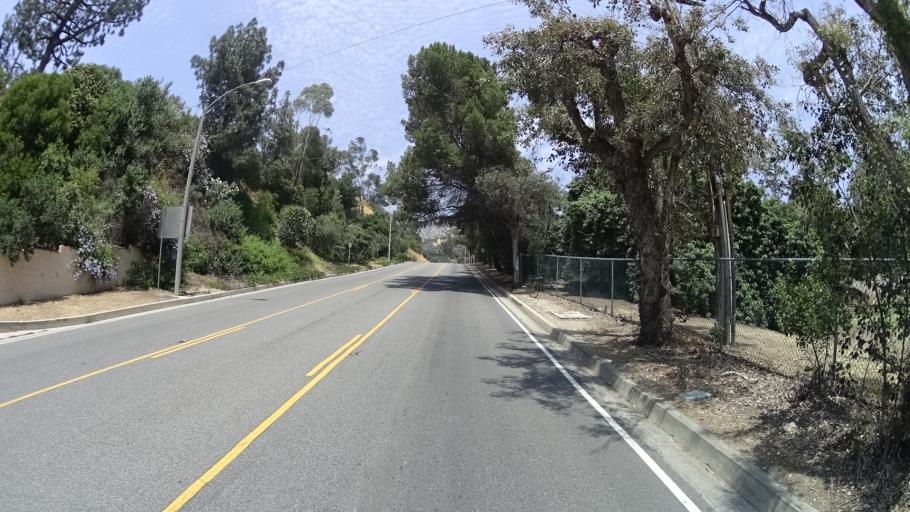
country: US
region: California
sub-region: Los Angeles County
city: Burbank
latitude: 34.1996
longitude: -118.3048
